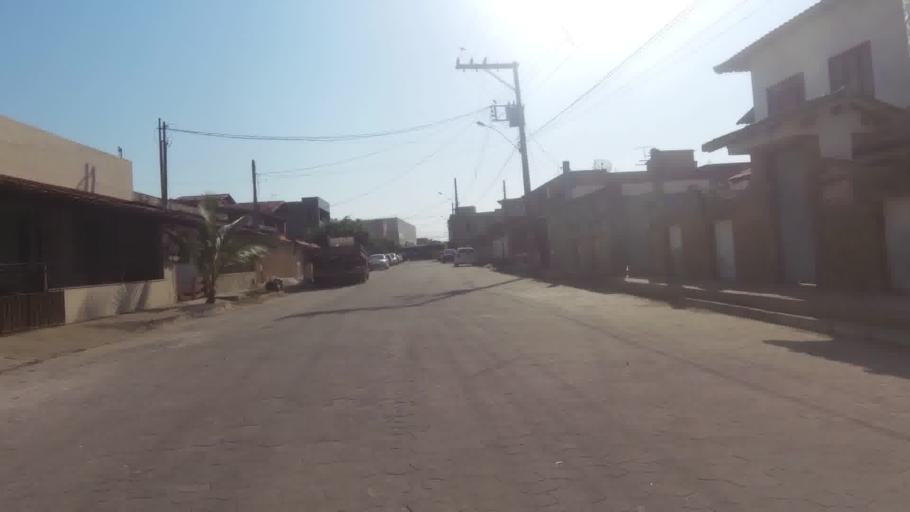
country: BR
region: Espirito Santo
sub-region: Itapemirim
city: Itapemirim
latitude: -21.0161
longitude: -40.8113
